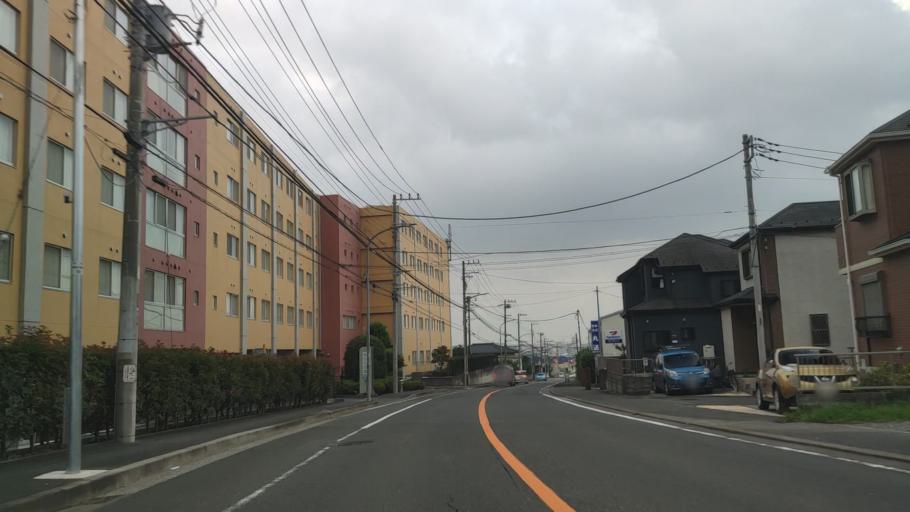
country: JP
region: Kanagawa
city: Minami-rinkan
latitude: 35.4254
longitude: 139.5019
